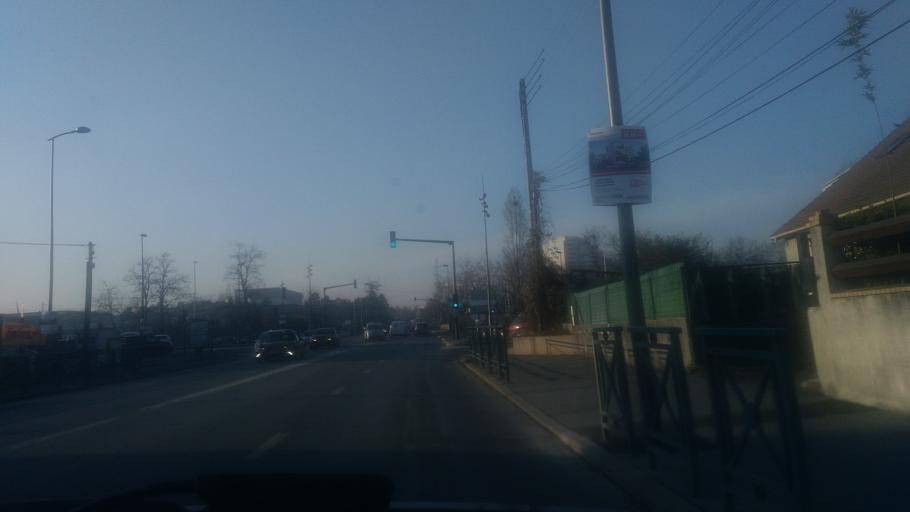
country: FR
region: Ile-de-France
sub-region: Departement du Val-d'Oise
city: Cergy-Pontoise
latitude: 49.0470
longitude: 2.0823
